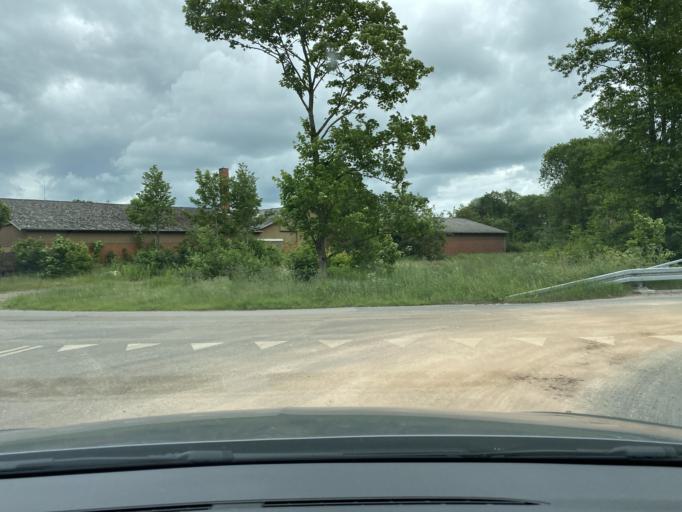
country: DK
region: South Denmark
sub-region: Vejle Kommune
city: Vejle
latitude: 55.6634
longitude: 9.4903
